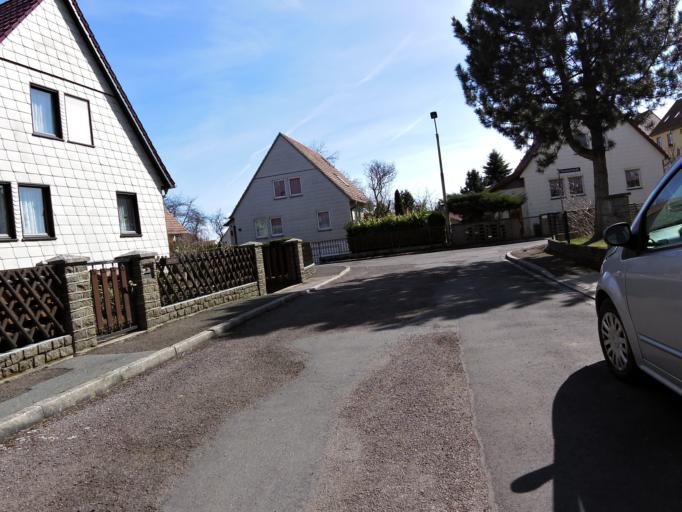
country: DE
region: Saxony
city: Borsdorf
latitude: 51.3397
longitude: 12.4915
